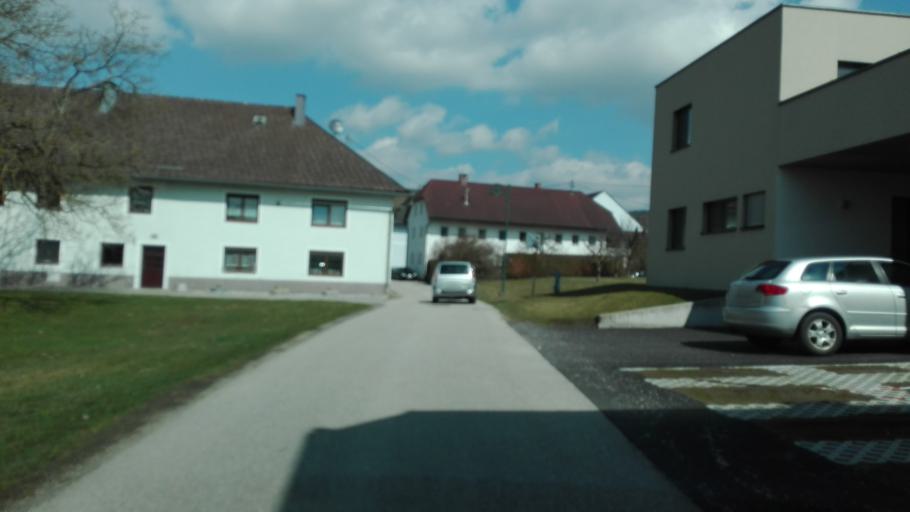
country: AT
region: Upper Austria
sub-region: Politischer Bezirk Urfahr-Umgebung
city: Feldkirchen an der Donau
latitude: 48.3573
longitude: 14.0287
